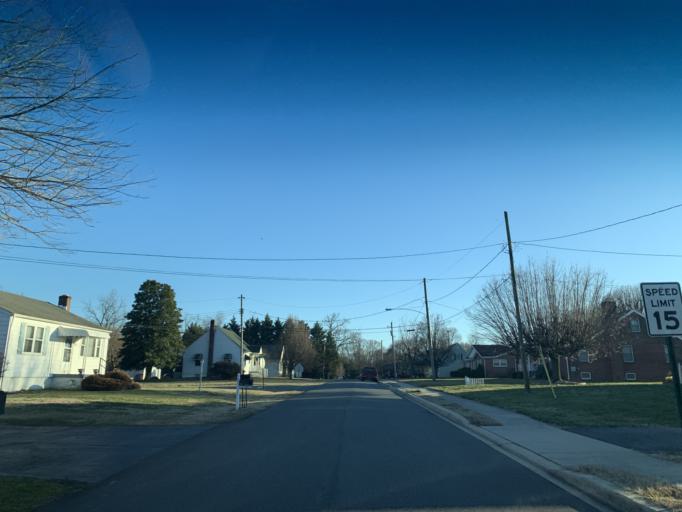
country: US
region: Maryland
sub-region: Cecil County
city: Perryville
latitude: 39.5641
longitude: -76.0683
